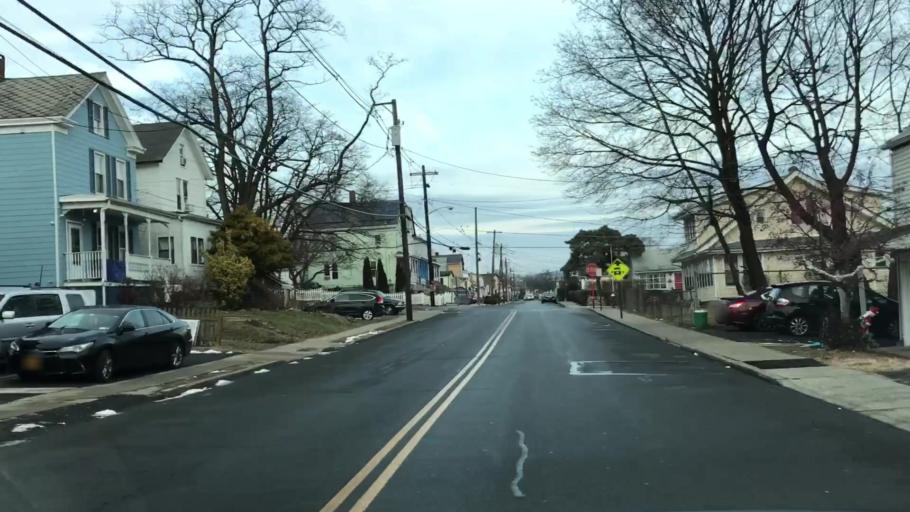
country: US
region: New York
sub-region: Rockland County
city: Haverstraw
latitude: 41.1936
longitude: -73.9631
